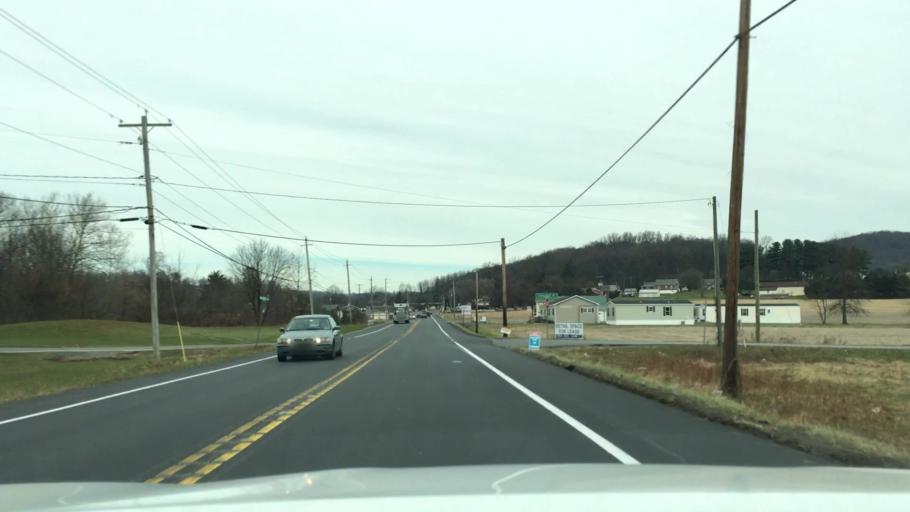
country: US
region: Pennsylvania
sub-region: Berks County
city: Bally
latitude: 40.4433
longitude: -75.5545
